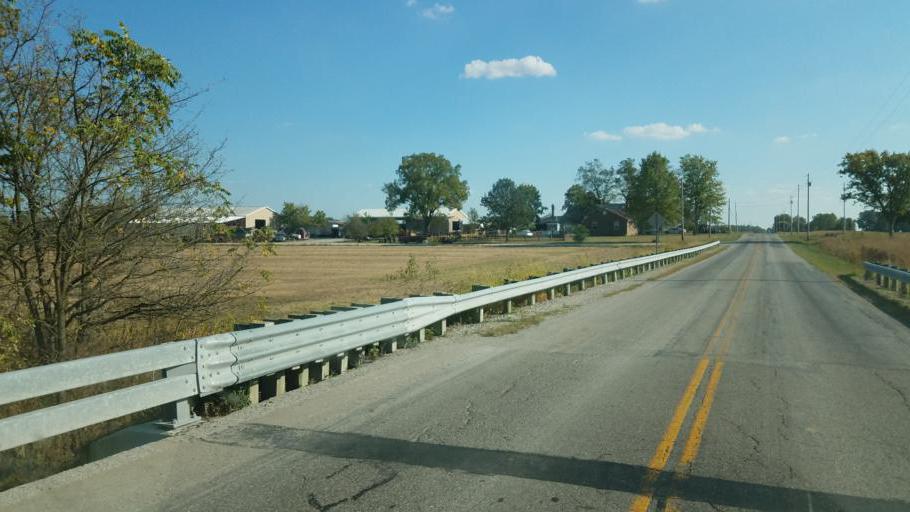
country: US
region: Ohio
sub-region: Union County
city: Richwood
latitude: 40.5590
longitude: -83.3917
